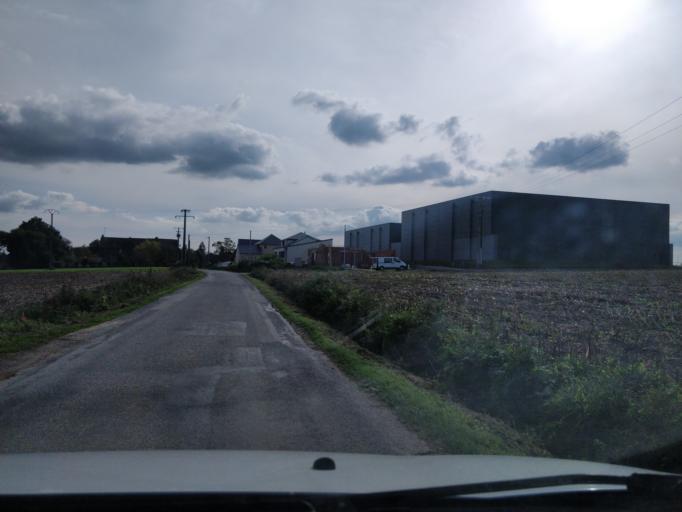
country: FR
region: Brittany
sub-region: Departement d'Ille-et-Vilaine
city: Chateaubourg
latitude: 48.1176
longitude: -1.3815
